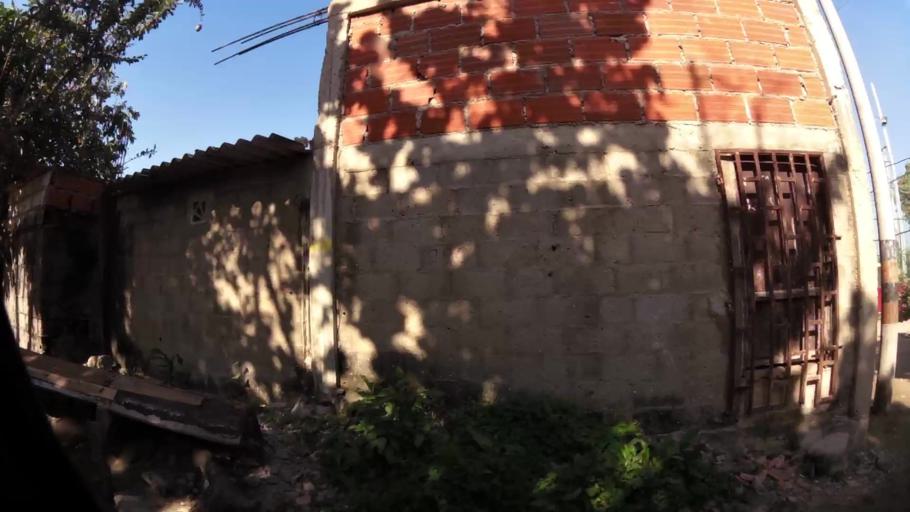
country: CO
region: Bolivar
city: Cartagena
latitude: 10.4841
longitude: -75.4907
